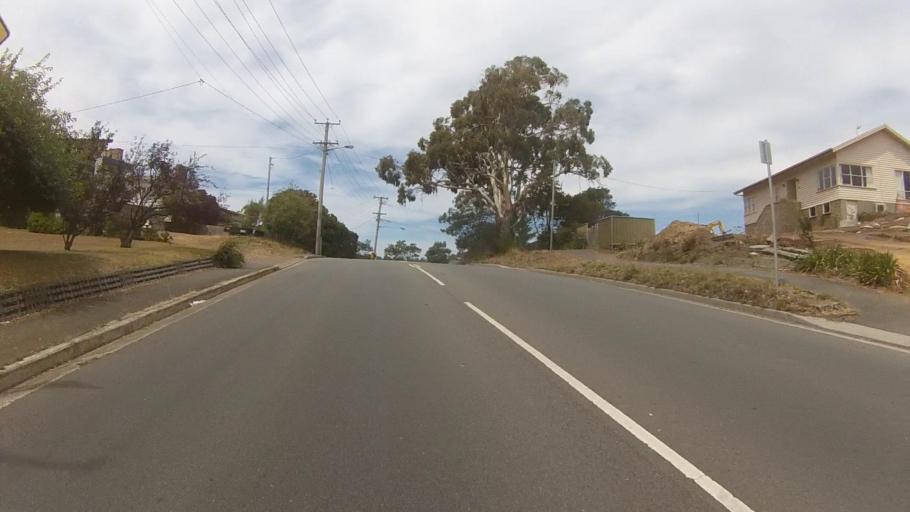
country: AU
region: Tasmania
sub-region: Clarence
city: Warrane
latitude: -42.8552
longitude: 147.3719
